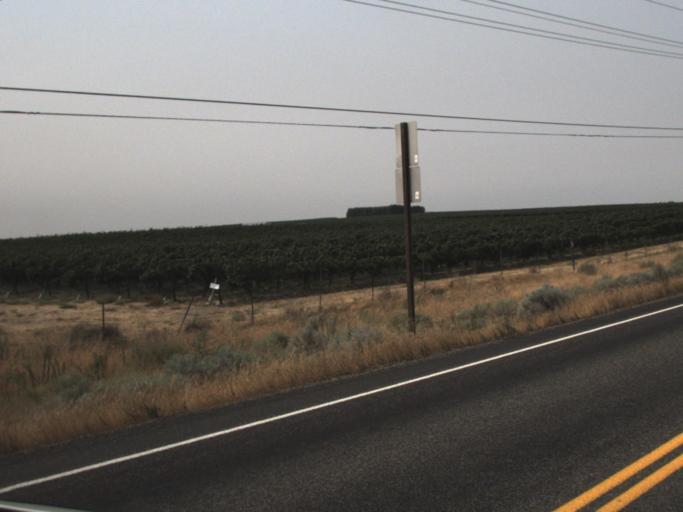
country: US
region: Oregon
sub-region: Morrow County
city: Irrigon
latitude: 45.9433
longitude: -119.6030
